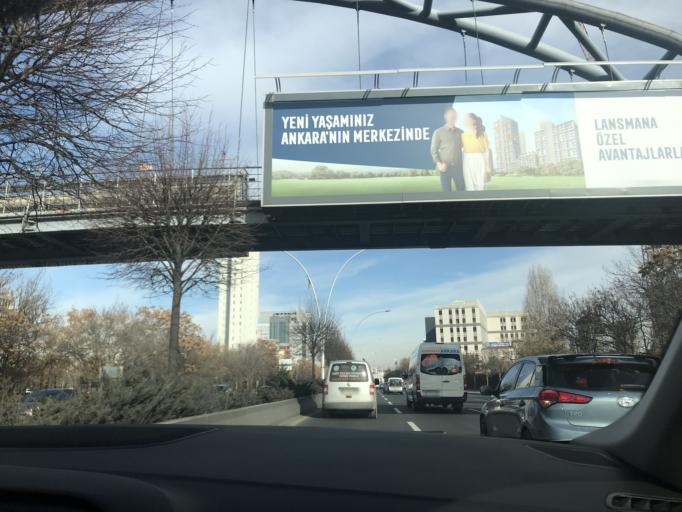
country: TR
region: Ankara
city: Ankara
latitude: 39.9357
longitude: 32.8226
